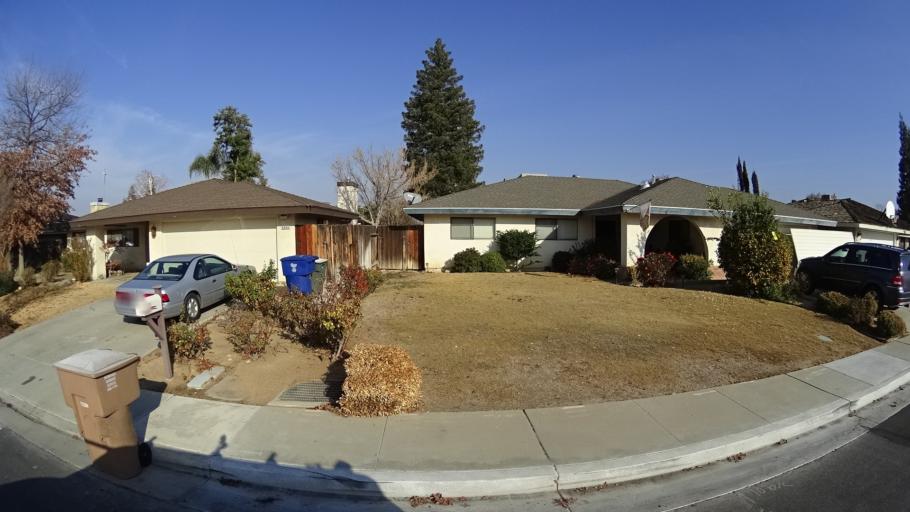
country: US
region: California
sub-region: Kern County
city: Oildale
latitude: 35.4045
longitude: -118.9260
